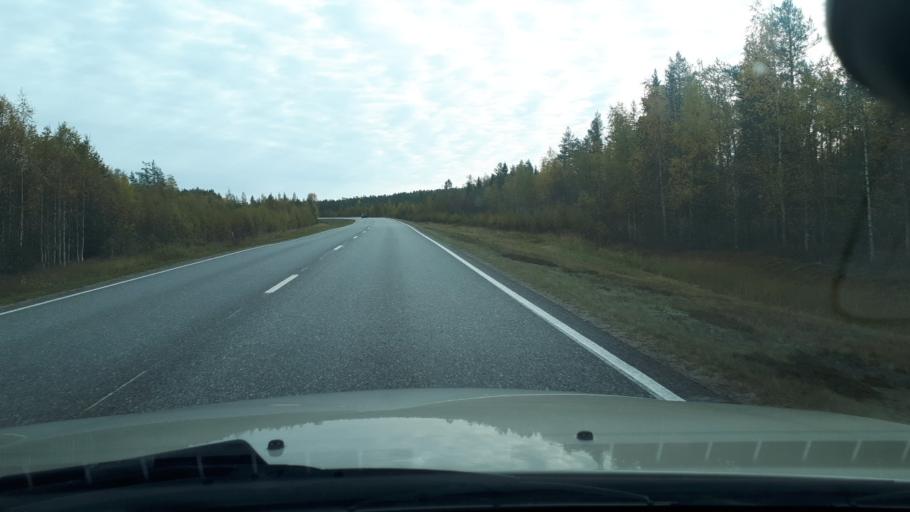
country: FI
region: Lapland
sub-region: Rovaniemi
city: Ranua
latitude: 65.9484
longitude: 26.4370
